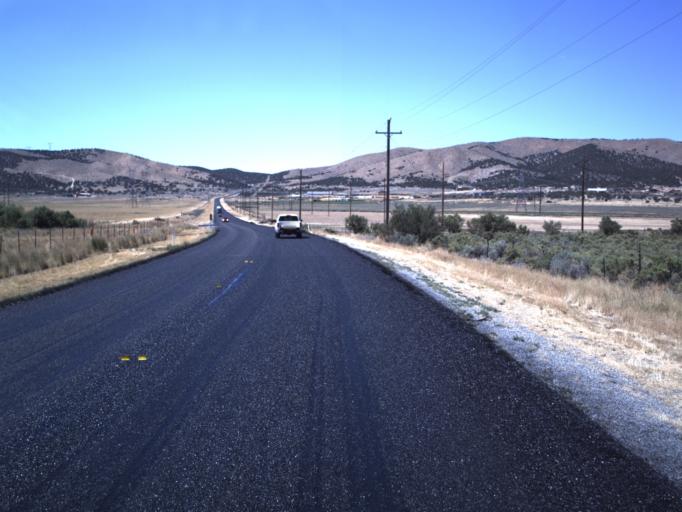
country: US
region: Utah
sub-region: Juab County
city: Nephi
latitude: 39.7099
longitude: -111.8984
